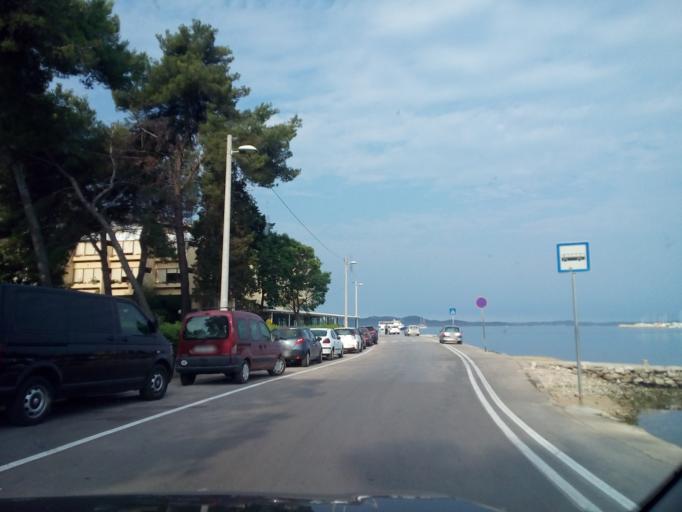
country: HR
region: Zadarska
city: Zadar
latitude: 44.1245
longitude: 15.2253
